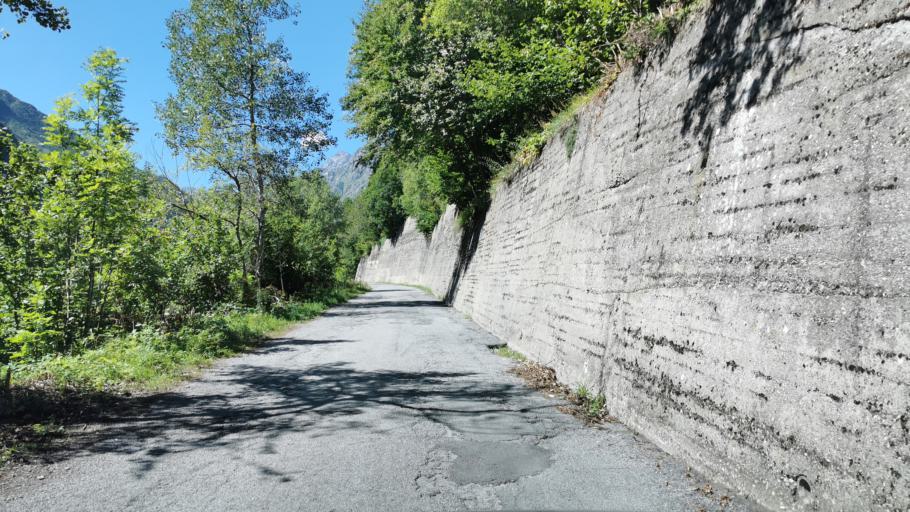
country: IT
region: Piedmont
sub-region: Provincia di Cuneo
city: Entracque
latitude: 44.2055
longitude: 7.3714
